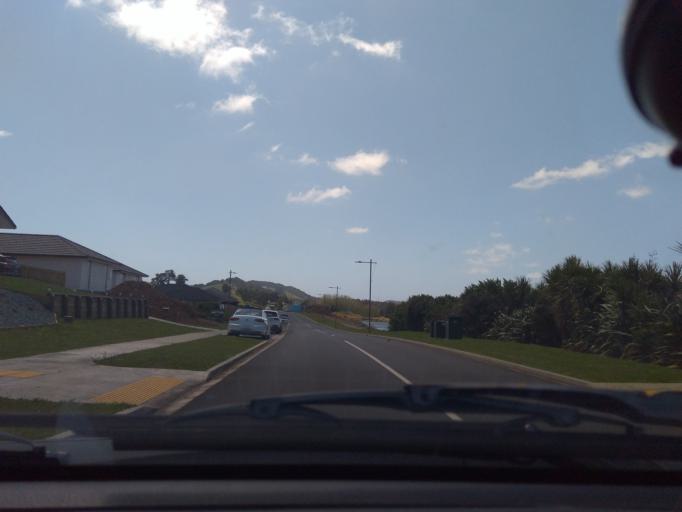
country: NZ
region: Northland
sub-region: Whangarei
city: Whangarei
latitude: -35.6768
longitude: 174.3184
